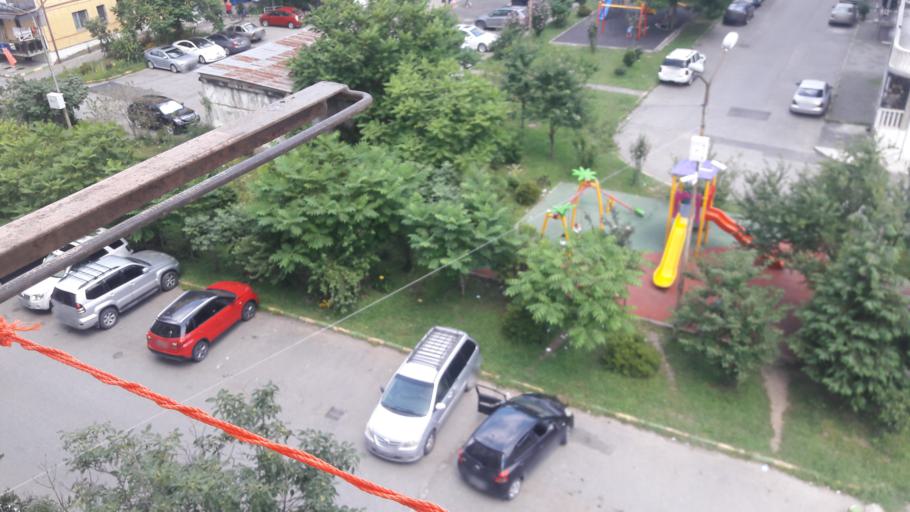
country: GE
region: Ajaria
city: Batumi
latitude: 41.6341
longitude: 41.6065
